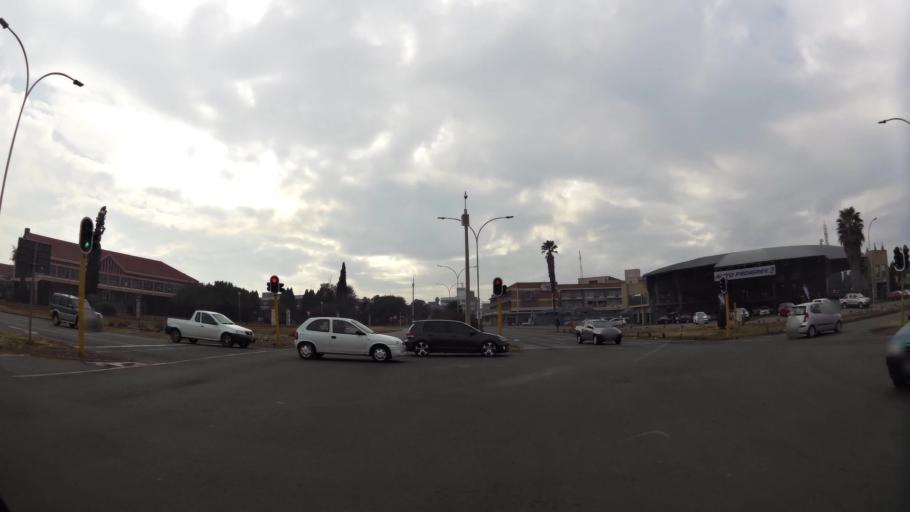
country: ZA
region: Gauteng
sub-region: Sedibeng District Municipality
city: Vanderbijlpark
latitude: -26.7015
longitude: 27.8335
